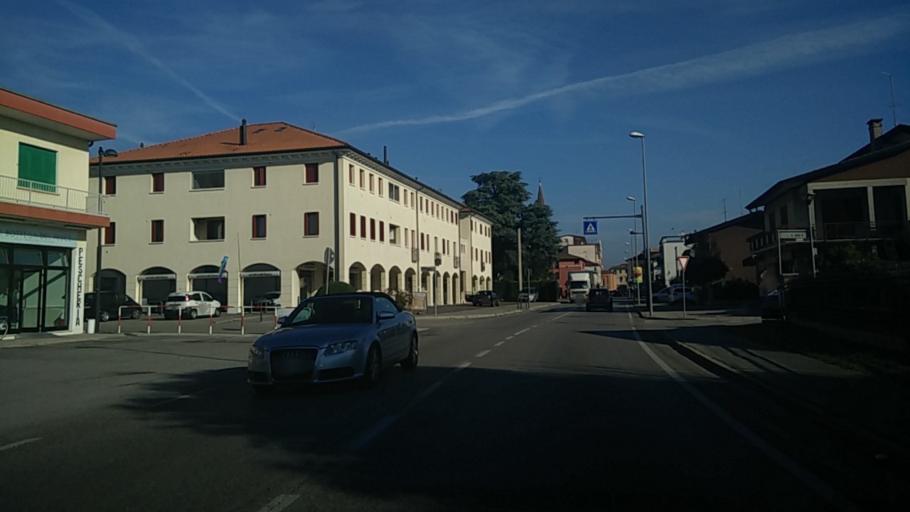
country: IT
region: Veneto
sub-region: Provincia di Padova
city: Trebaseleghe
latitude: 45.5881
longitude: 12.0512
